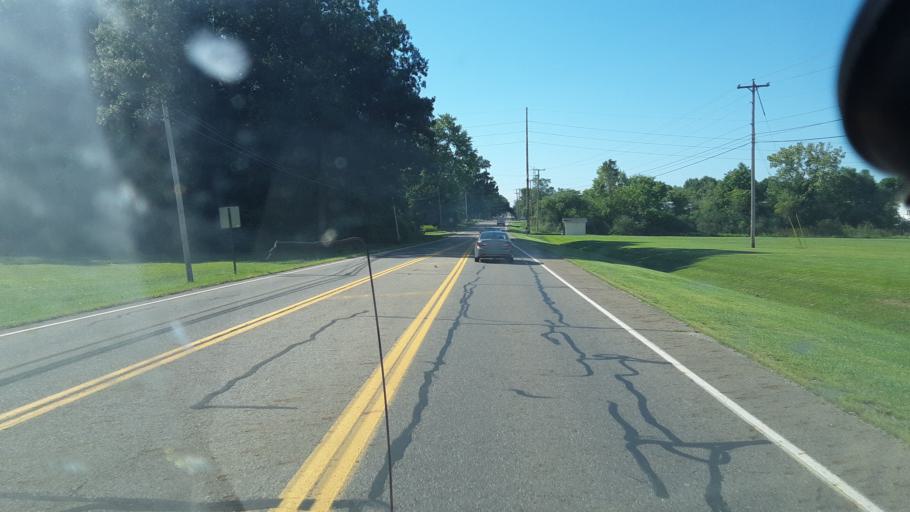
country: US
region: Ohio
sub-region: Portage County
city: Ravenna
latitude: 41.1325
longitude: -81.2420
